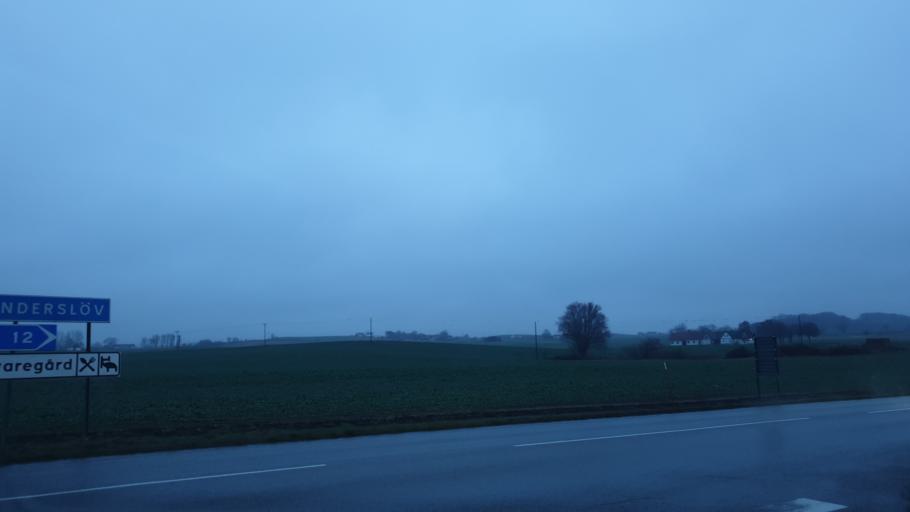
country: SE
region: Skane
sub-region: Skurups Kommun
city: Skivarp
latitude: 55.4185
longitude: 13.6367
